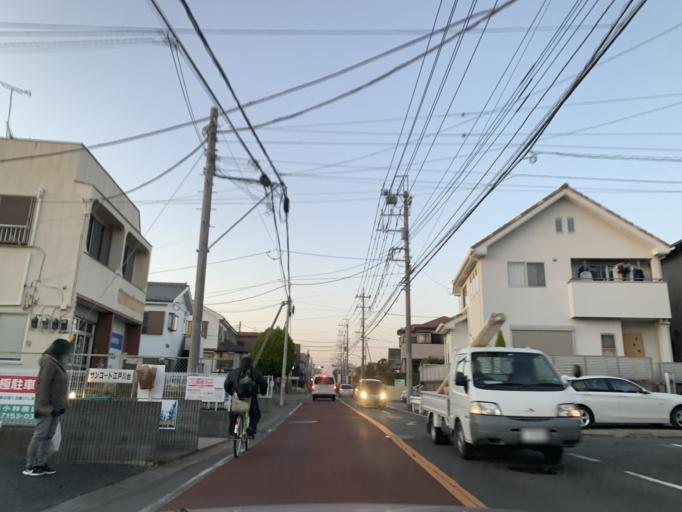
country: JP
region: Chiba
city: Nagareyama
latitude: 35.9007
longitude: 139.9070
